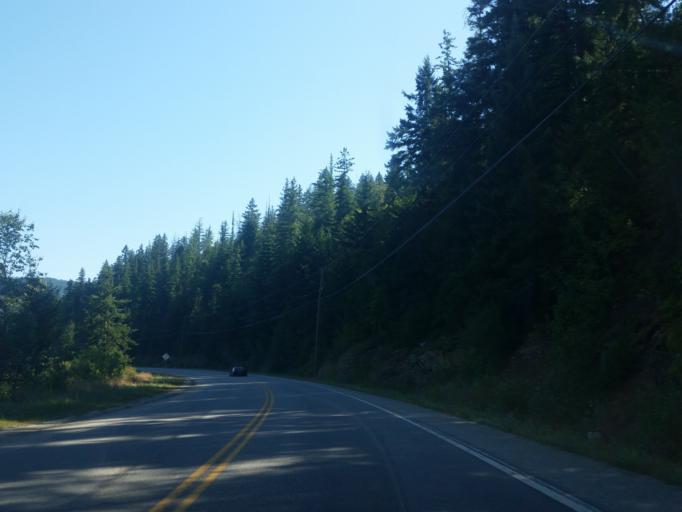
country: CA
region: British Columbia
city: Sicamous
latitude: 50.7891
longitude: -118.9919
